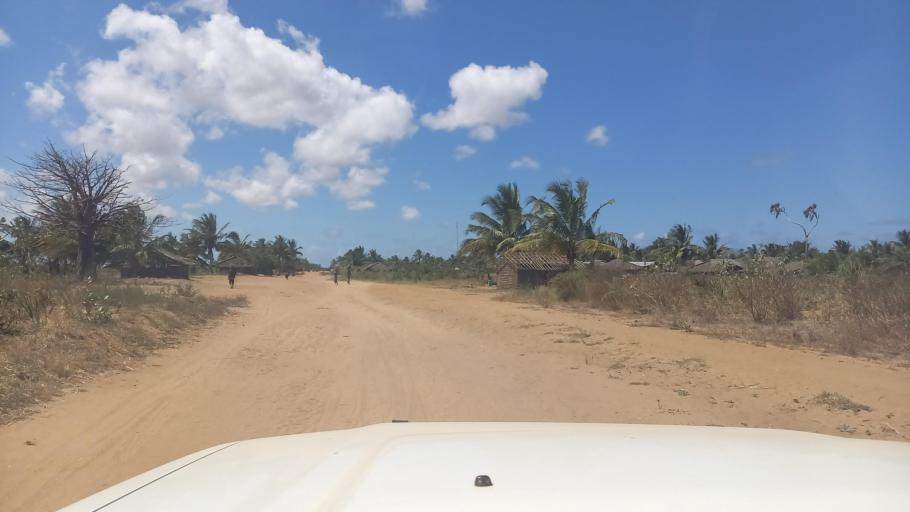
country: MZ
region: Cabo Delgado
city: Pemba
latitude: -13.4214
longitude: 40.5185
